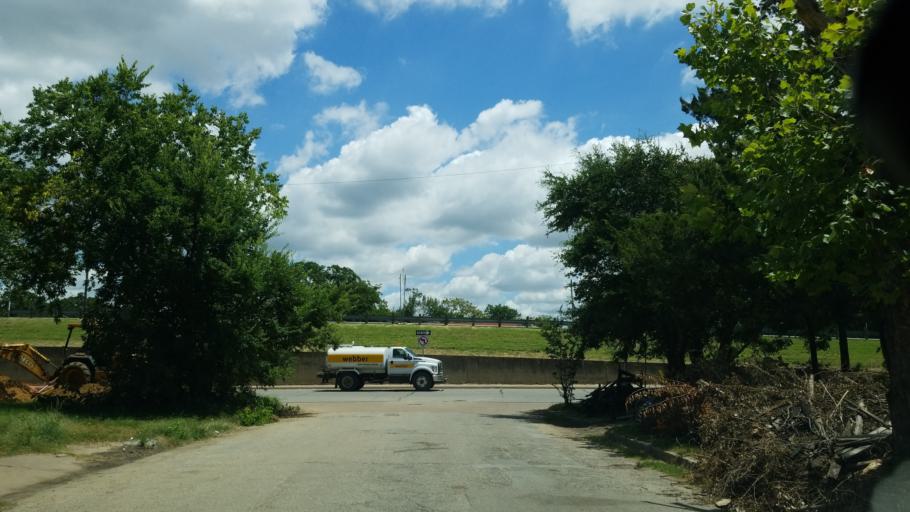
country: US
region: Texas
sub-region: Dallas County
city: Dallas
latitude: 32.7523
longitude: -96.7646
